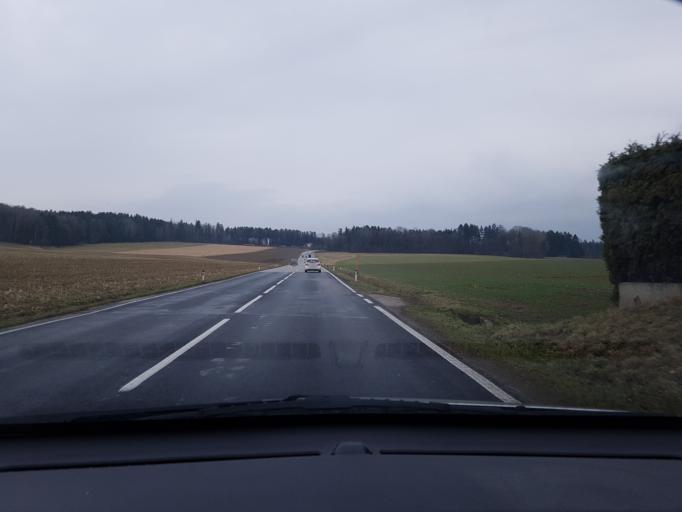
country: AT
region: Upper Austria
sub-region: Steyr Stadt
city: Steyr
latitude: 48.0685
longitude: 14.3845
